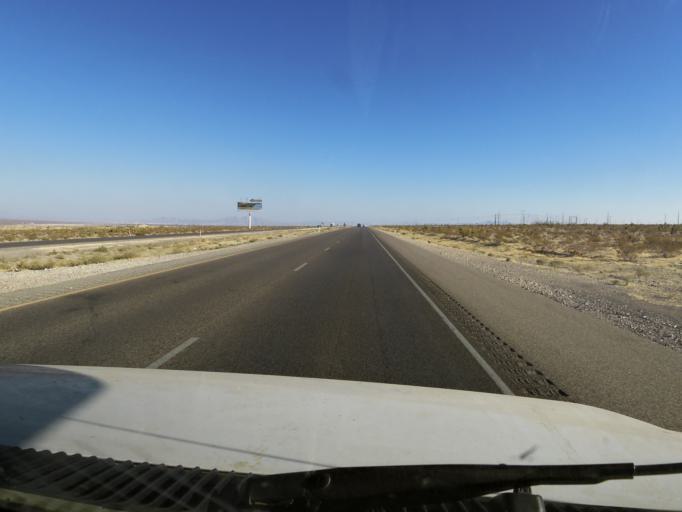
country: US
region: Nevada
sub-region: Clark County
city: Summerlin South
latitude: 36.3518
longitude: -115.3392
